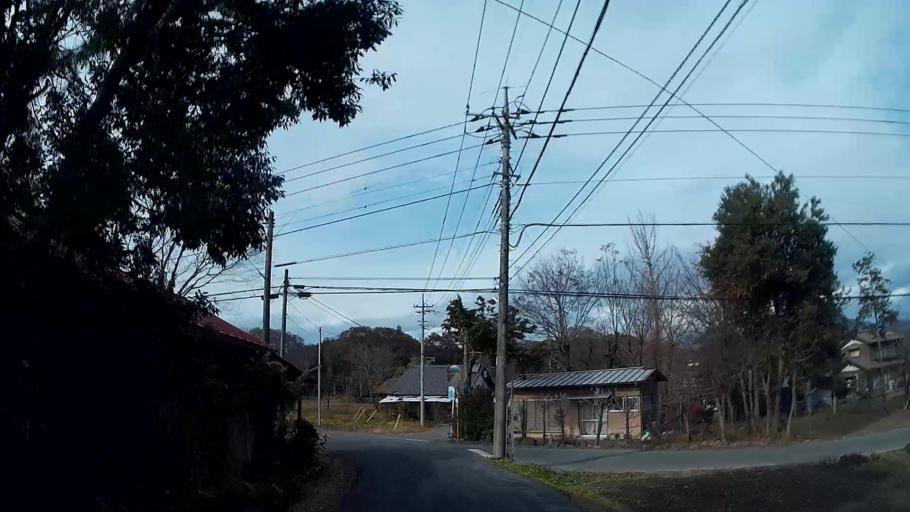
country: JP
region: Saitama
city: Chichibu
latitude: 36.0110
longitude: 139.0417
